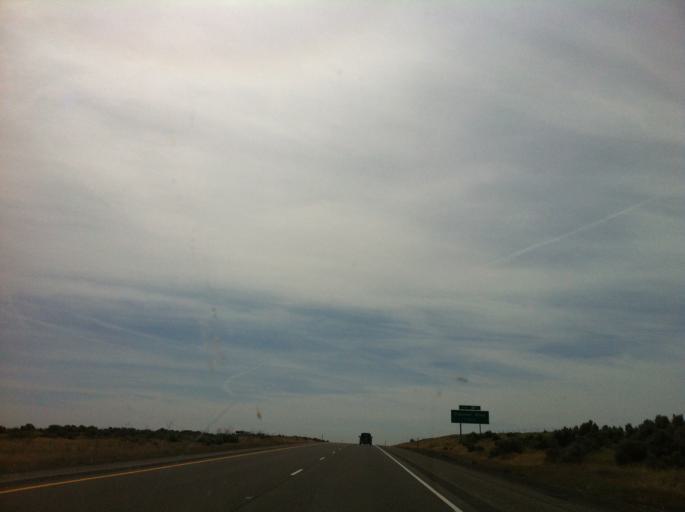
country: US
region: Oregon
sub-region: Malheur County
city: Ontario
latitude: 44.0961
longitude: -117.0347
